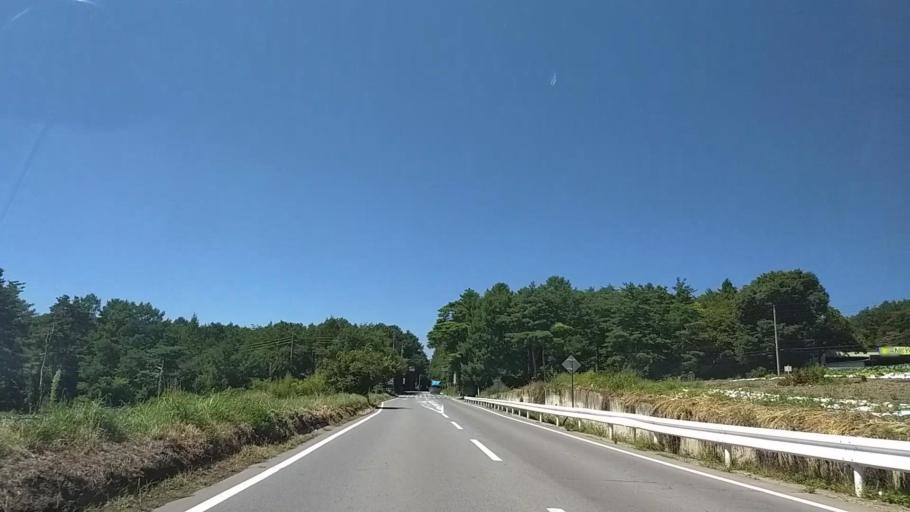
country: JP
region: Nagano
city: Komoro
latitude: 36.3410
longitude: 138.4699
